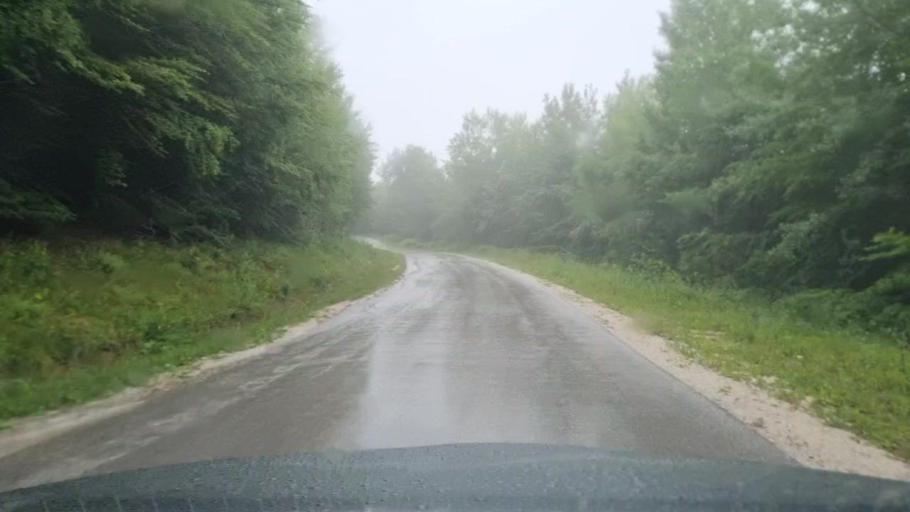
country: BA
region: Republika Srpska
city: Koran
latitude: 43.6469
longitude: 18.6061
